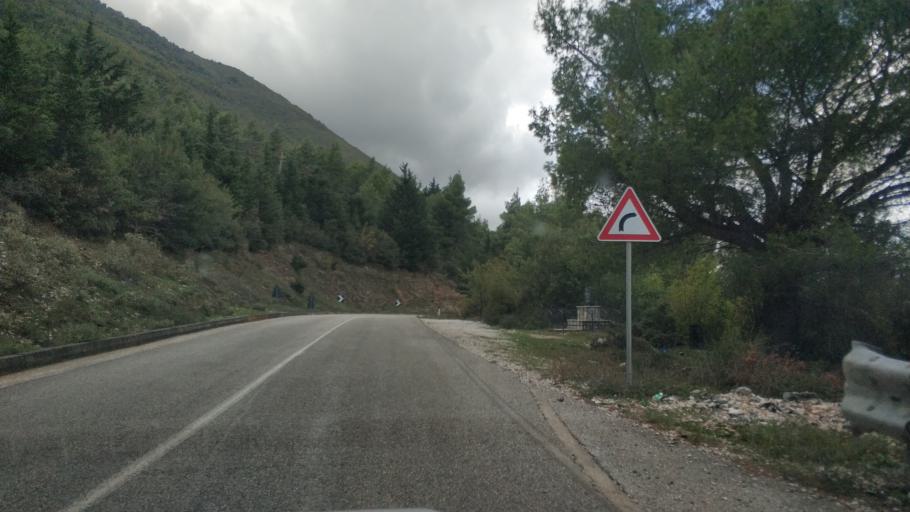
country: AL
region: Vlore
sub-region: Rrethi i Vlores
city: Orikum
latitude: 40.2512
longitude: 19.5399
